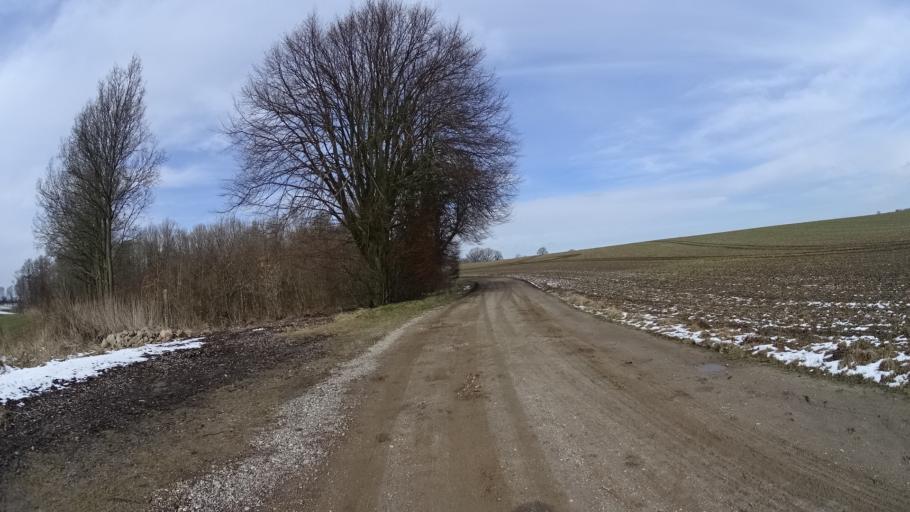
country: DE
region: Schleswig-Holstein
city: Loptin
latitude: 54.1629
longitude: 10.2287
